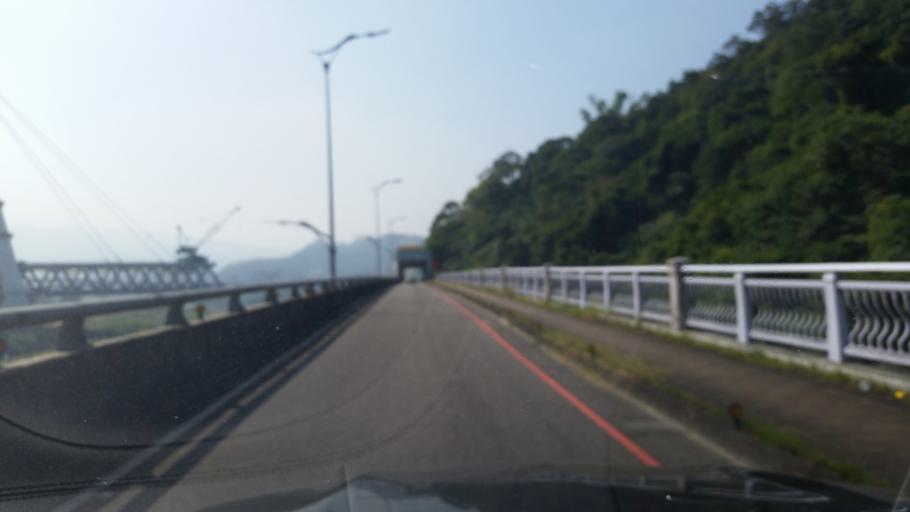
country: TW
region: Taipei
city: Taipei
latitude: 24.9884
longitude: 121.5257
